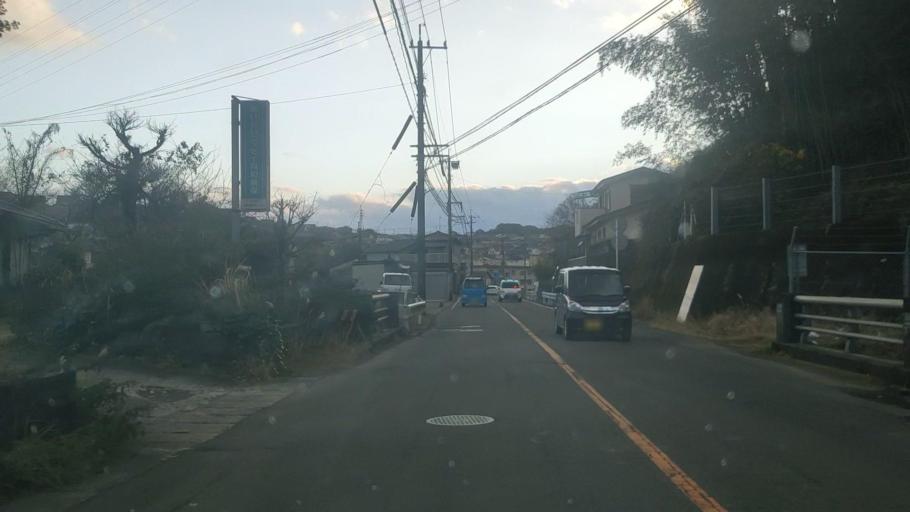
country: JP
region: Kagoshima
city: Kagoshima-shi
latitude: 31.6247
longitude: 130.5429
